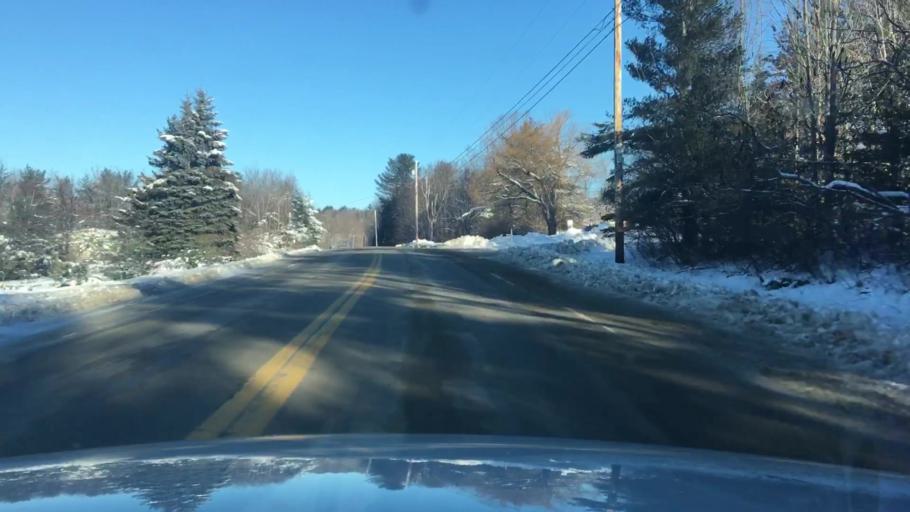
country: US
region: Maine
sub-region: Kennebec County
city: Readfield
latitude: 44.4457
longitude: -69.9685
